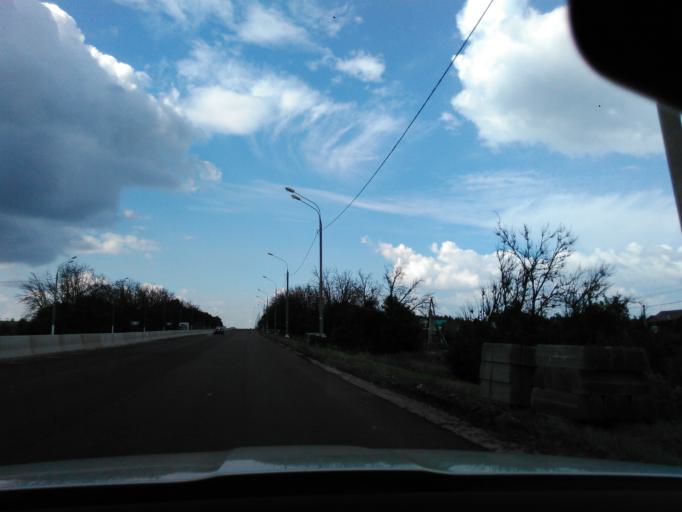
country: RU
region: Moskovskaya
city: Lozhki
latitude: 56.1090
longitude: 37.0923
